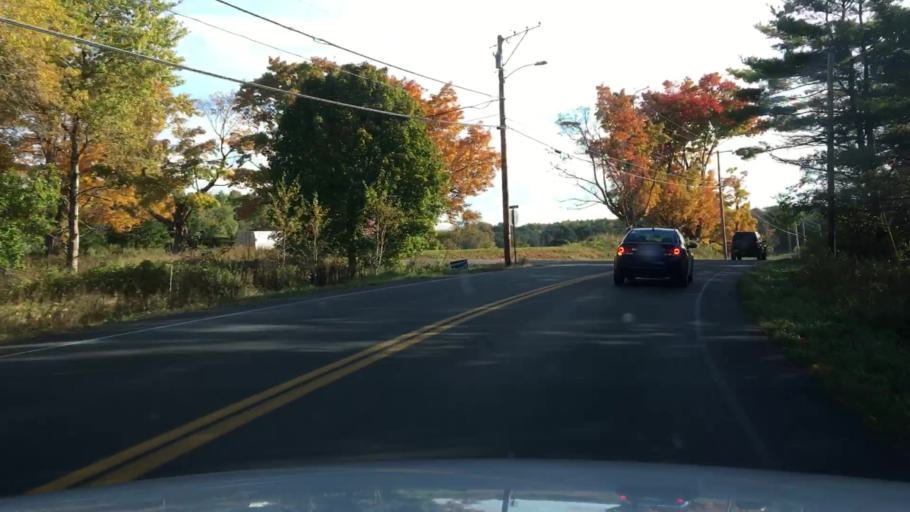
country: US
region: Maine
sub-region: Knox County
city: Thomaston
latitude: 44.0938
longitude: -69.1585
